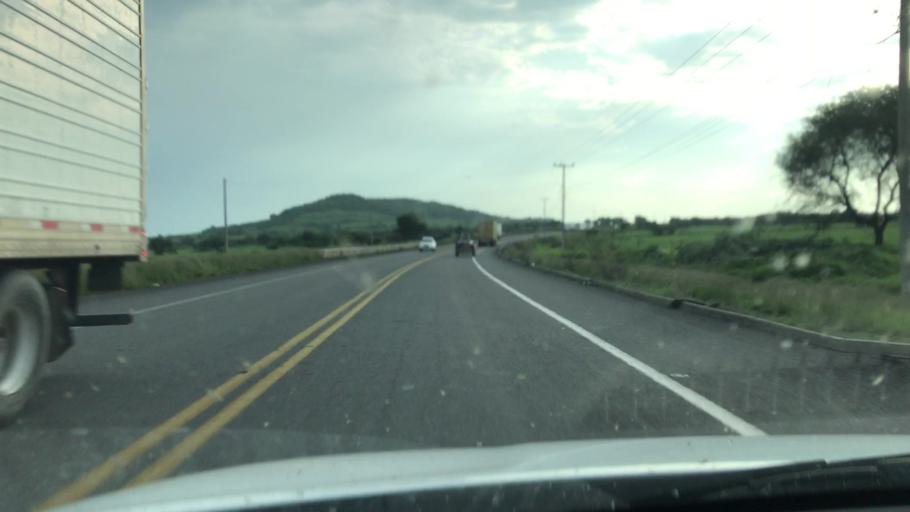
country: MX
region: Michoacan
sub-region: Yurecuaro
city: Yurecuaro
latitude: 20.3381
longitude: -102.1880
